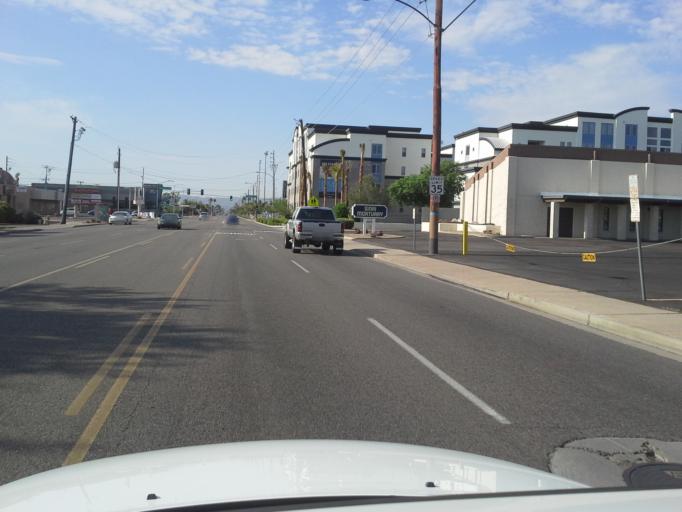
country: US
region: Arizona
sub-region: Maricopa County
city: Phoenix
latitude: 33.5035
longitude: -112.0476
